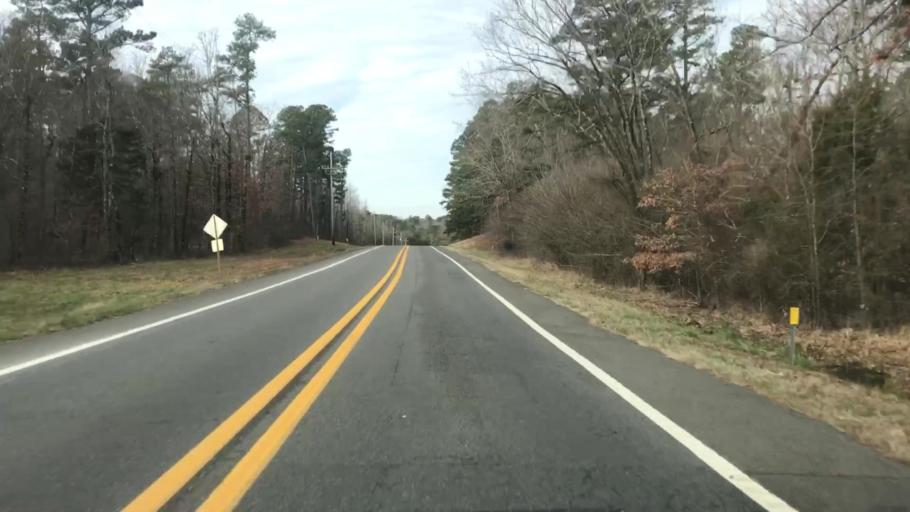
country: US
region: Arkansas
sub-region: Montgomery County
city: Mount Ida
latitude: 34.6086
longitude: -93.6776
